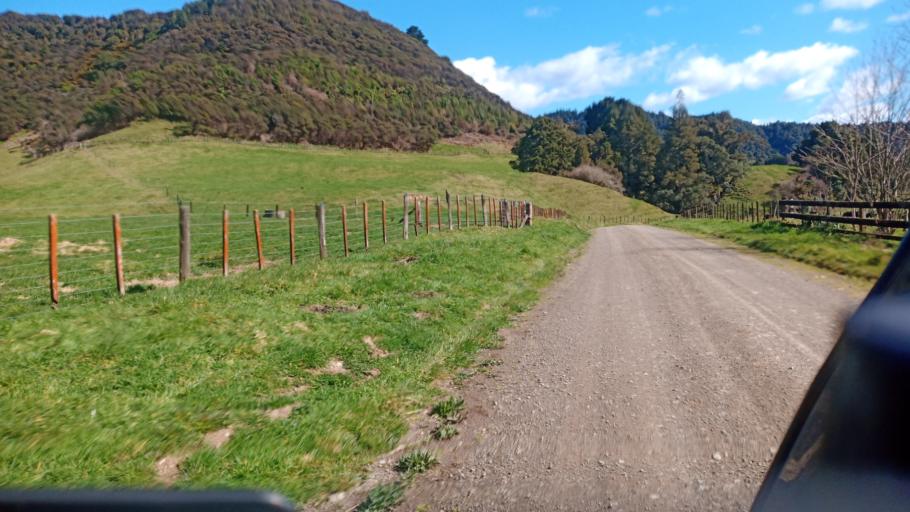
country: NZ
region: Bay of Plenty
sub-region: Opotiki District
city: Opotiki
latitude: -38.1118
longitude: 177.5170
